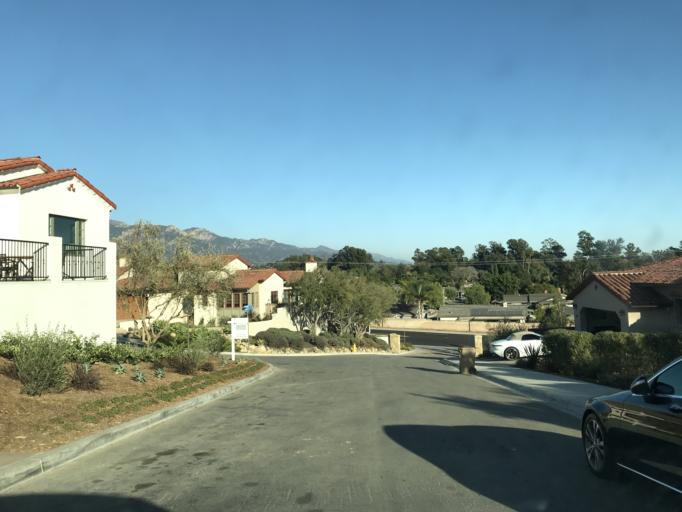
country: US
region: California
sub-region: Santa Barbara County
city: Goleta
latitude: 34.4464
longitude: -119.8086
